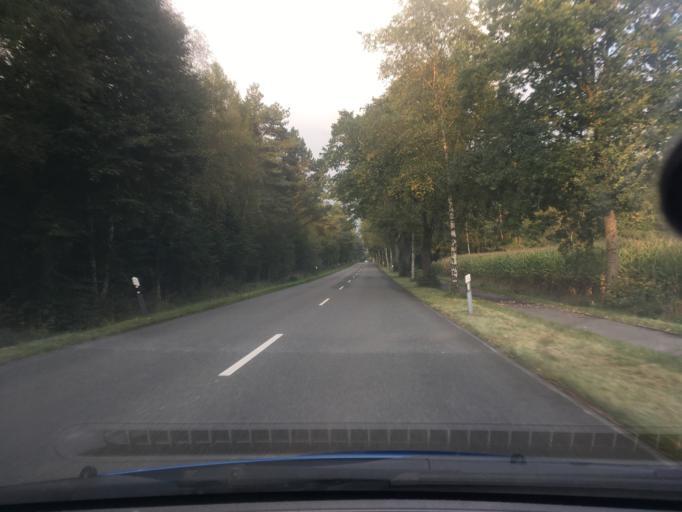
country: DE
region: Lower Saxony
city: Soderstorf
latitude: 53.1196
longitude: 10.0930
